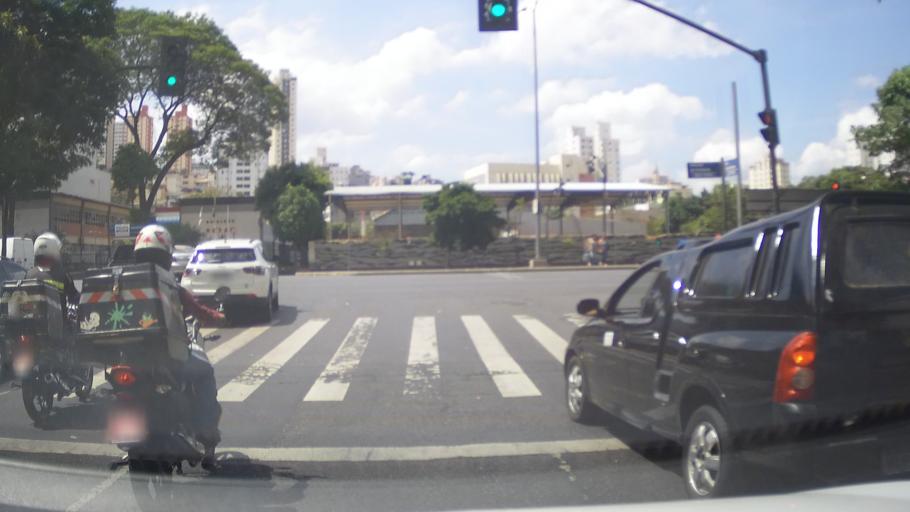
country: BR
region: Minas Gerais
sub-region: Belo Horizonte
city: Belo Horizonte
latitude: -19.9148
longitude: -43.9355
